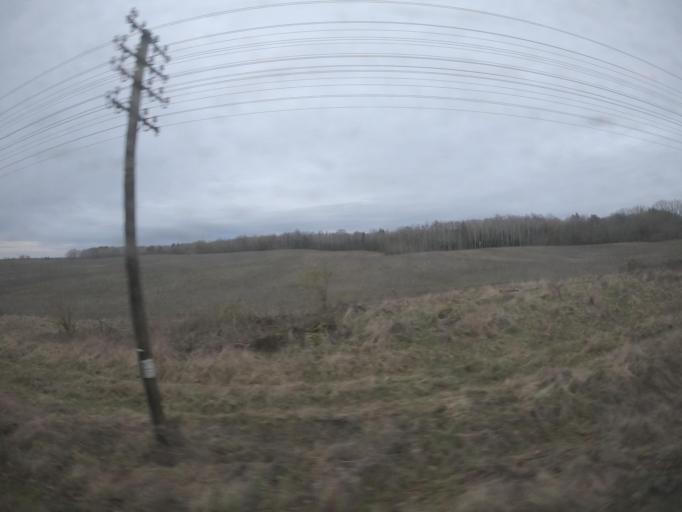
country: PL
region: West Pomeranian Voivodeship
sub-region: Powiat szczecinecki
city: Borne Sulinowo
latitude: 53.6552
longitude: 16.5833
